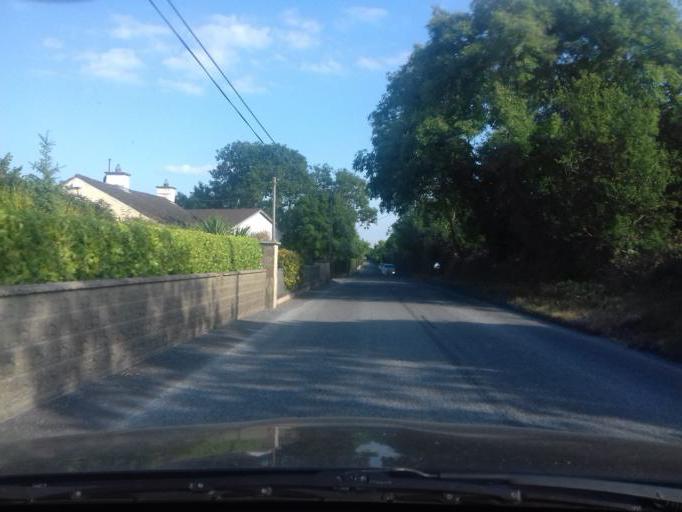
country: IE
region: Leinster
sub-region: Fingal County
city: Blanchardstown
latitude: 53.4431
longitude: -6.3873
